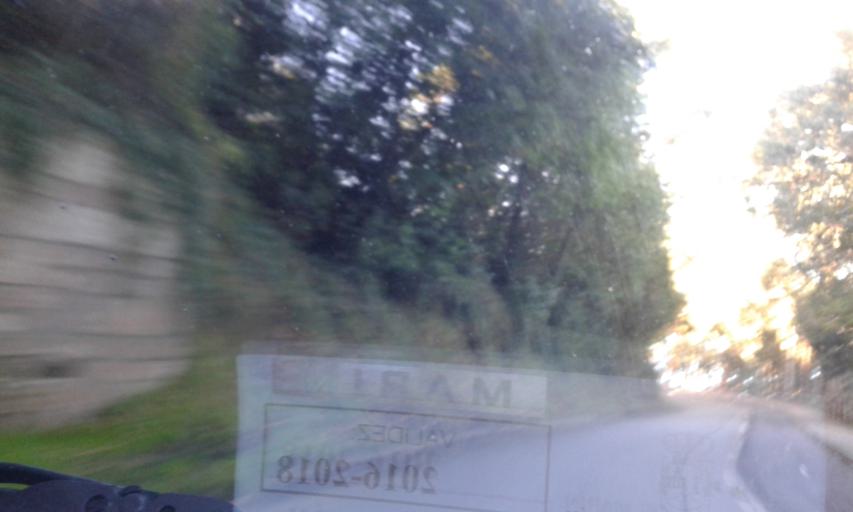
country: ES
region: Galicia
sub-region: Provincia de Pontevedra
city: Marin
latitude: 42.3846
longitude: -8.7242
